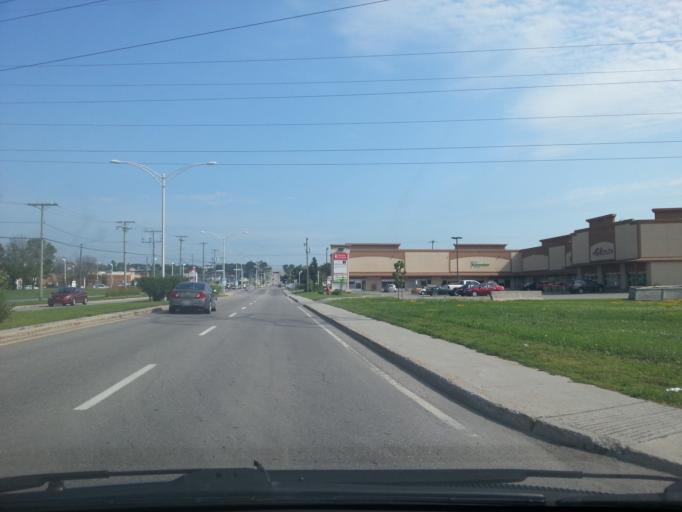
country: CA
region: Quebec
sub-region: Outaouais
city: Gatineau
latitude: 45.4889
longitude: -75.6750
